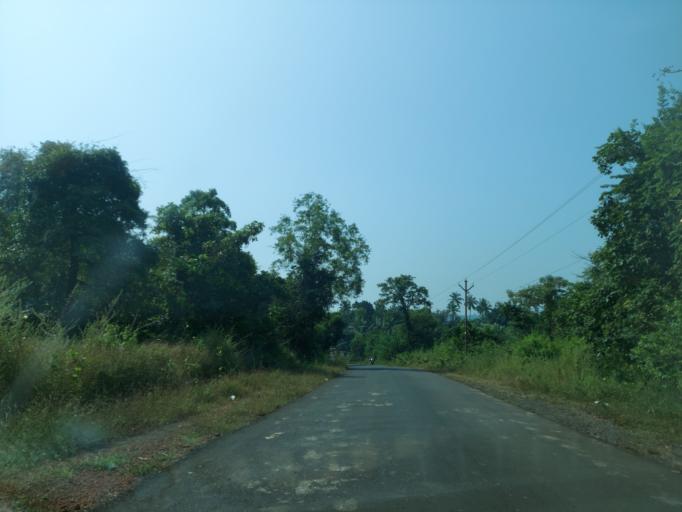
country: IN
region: Maharashtra
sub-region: Sindhudurg
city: Kudal
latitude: 15.9756
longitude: 73.6118
